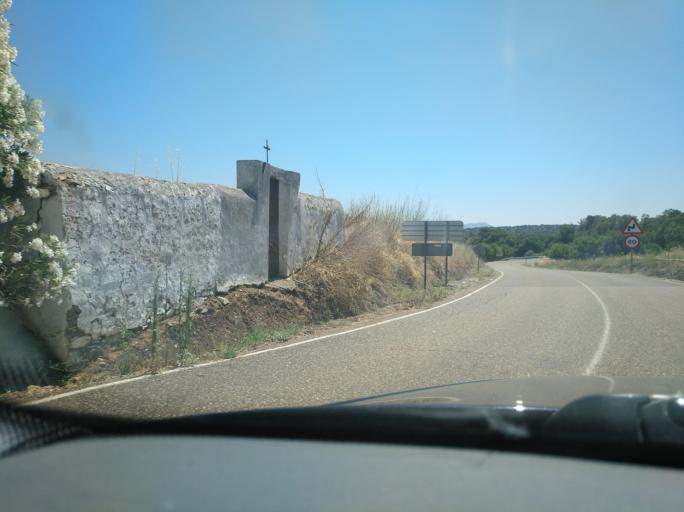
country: ES
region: Extremadura
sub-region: Provincia de Badajoz
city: Olivenza
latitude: 38.7253
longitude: -7.2131
